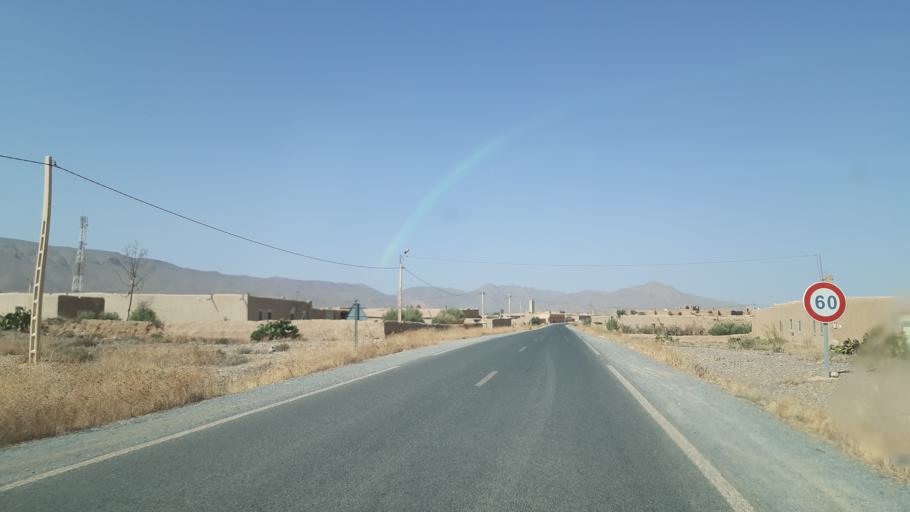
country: MA
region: Meknes-Tafilalet
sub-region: Errachidia
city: Amouguer
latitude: 32.2429
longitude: -4.5943
